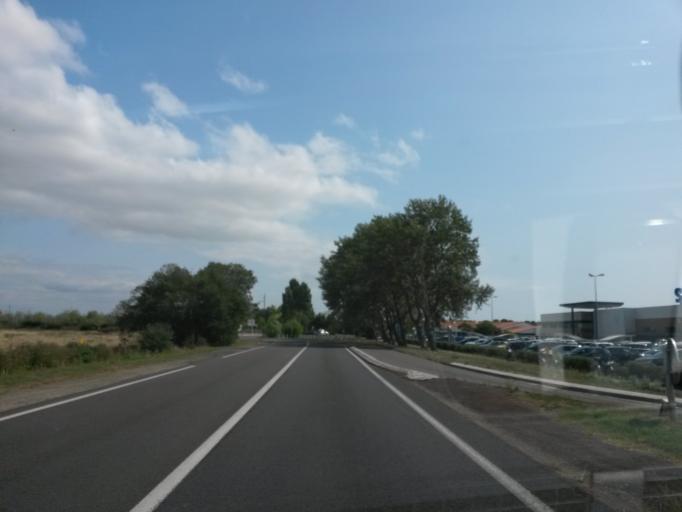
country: FR
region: Pays de la Loire
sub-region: Departement de la Vendee
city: La Tranche-sur-Mer
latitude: 46.3527
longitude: -1.4312
